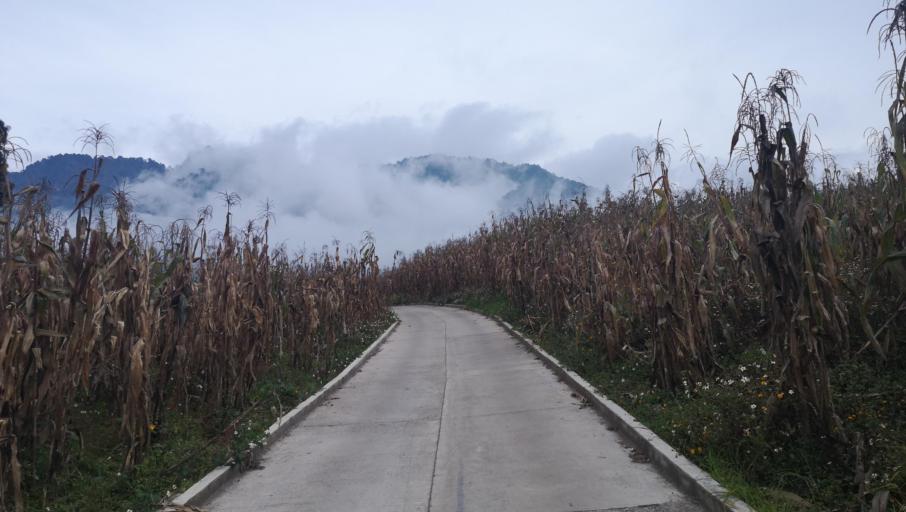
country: GT
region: Quetzaltenango
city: Cantel
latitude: 14.8186
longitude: -91.4371
